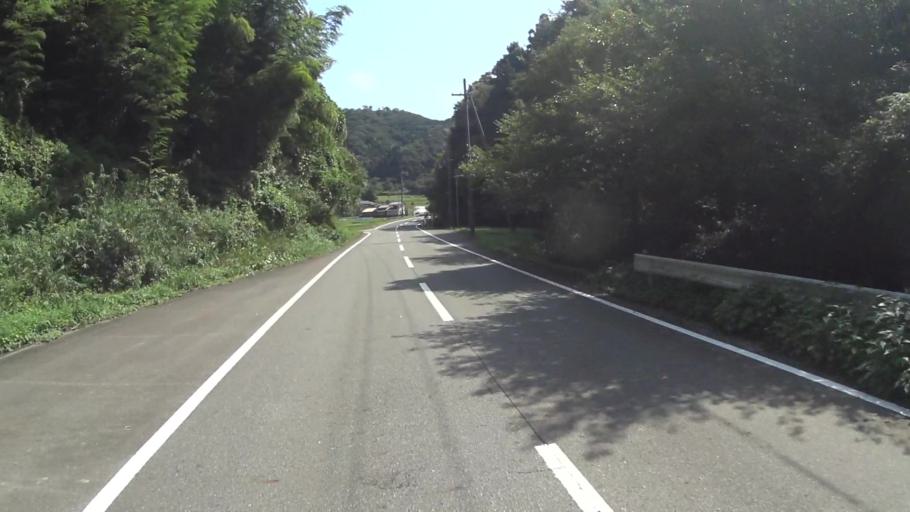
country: JP
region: Kyoto
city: Miyazu
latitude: 35.6838
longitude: 135.2648
